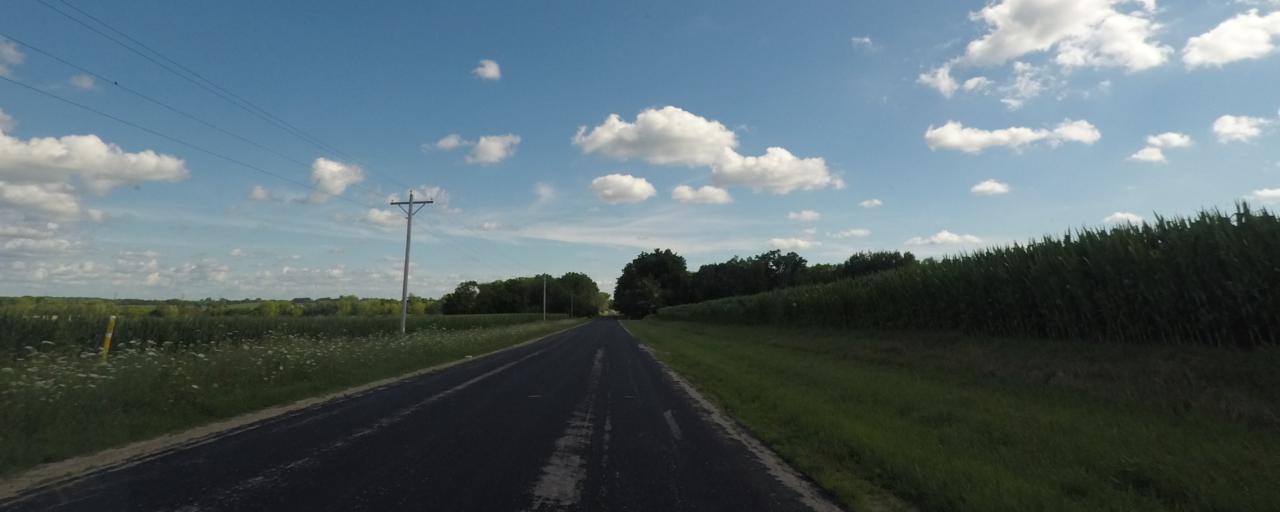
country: US
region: Wisconsin
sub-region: Rock County
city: Edgerton
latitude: 42.8561
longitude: -89.1320
